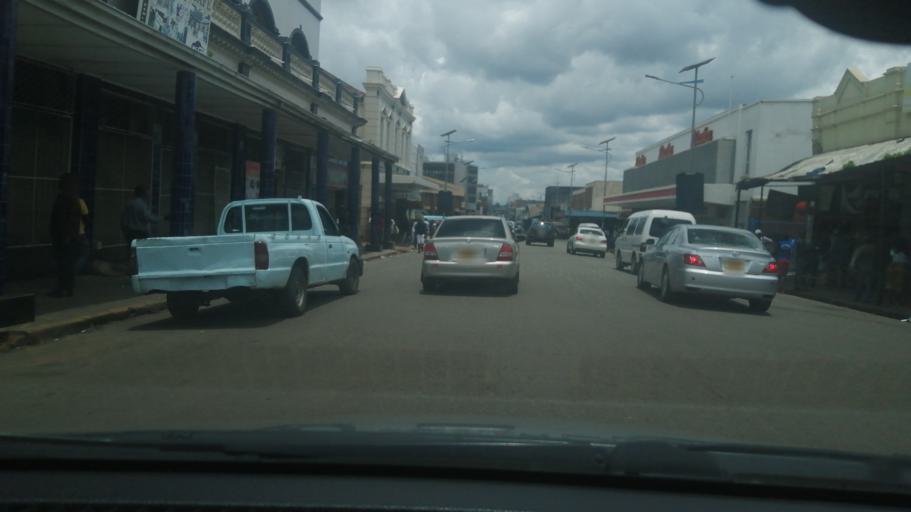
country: ZW
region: Harare
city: Harare
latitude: -17.8345
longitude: 31.0418
